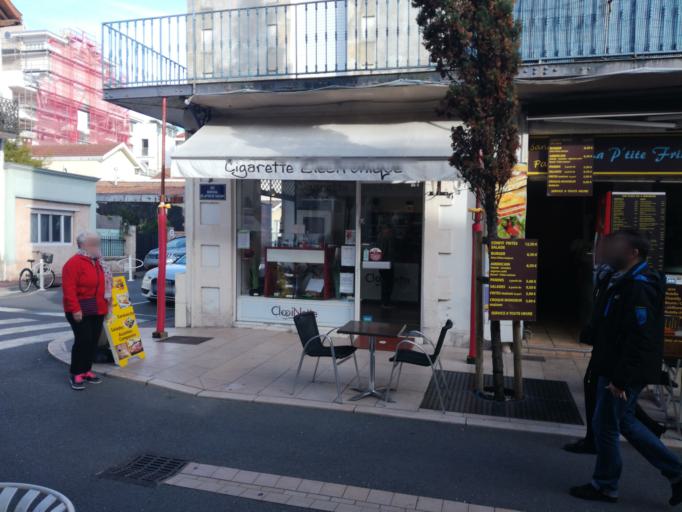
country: FR
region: Aquitaine
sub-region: Departement de la Gironde
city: Arcachon
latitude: 44.6618
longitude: -1.1725
